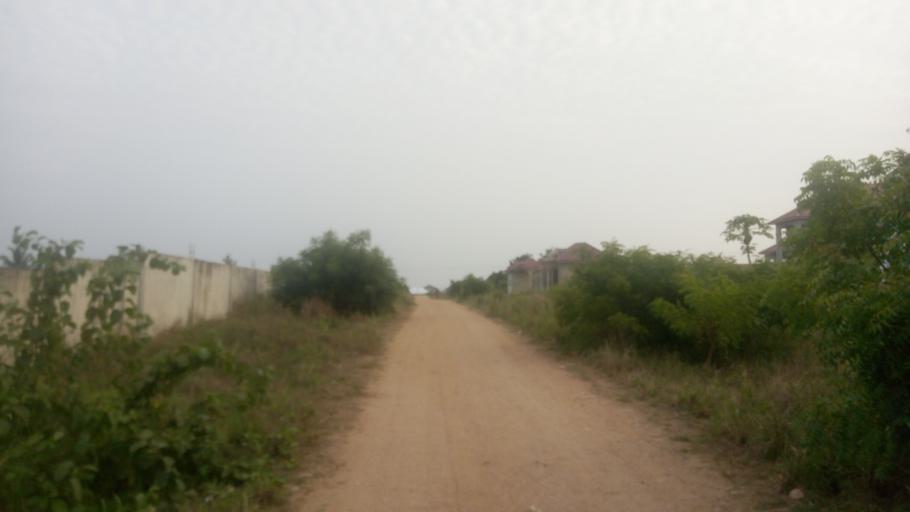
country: GH
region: Central
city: Winneba
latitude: 5.3793
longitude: -0.6287
